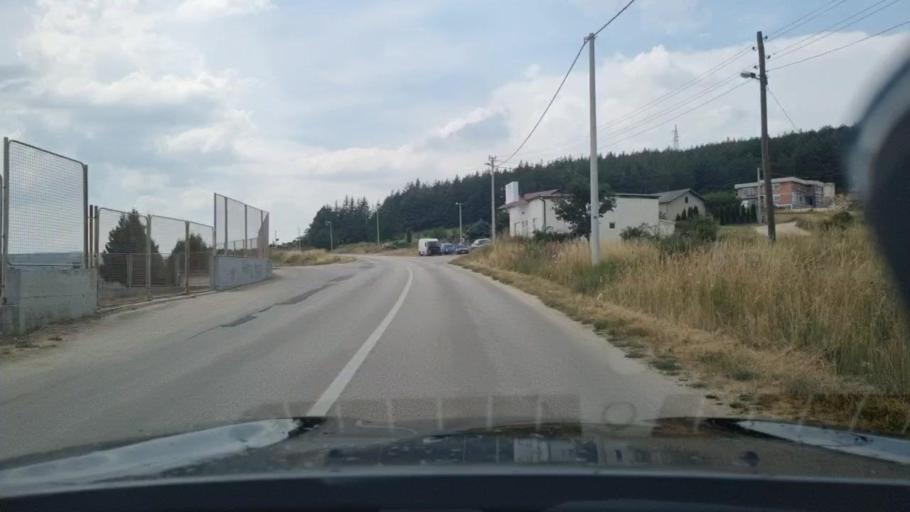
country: BA
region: Federation of Bosnia and Herzegovina
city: Tomislavgrad
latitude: 43.7039
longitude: 17.2120
